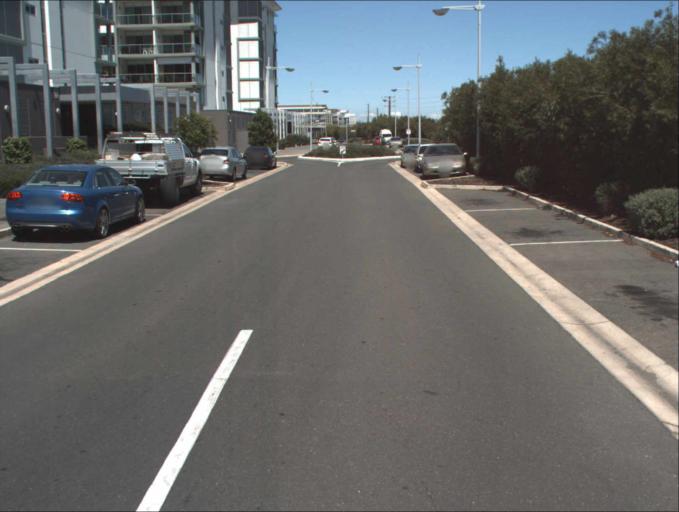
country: AU
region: South Australia
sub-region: Port Adelaide Enfield
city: Birkenhead
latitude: -34.8444
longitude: 138.4940
